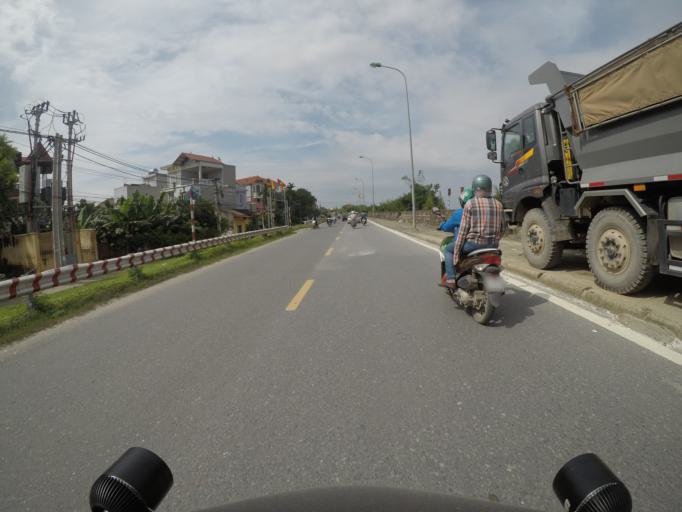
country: VN
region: Ha Noi
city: Tay Ho
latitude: 21.0936
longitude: 105.7739
